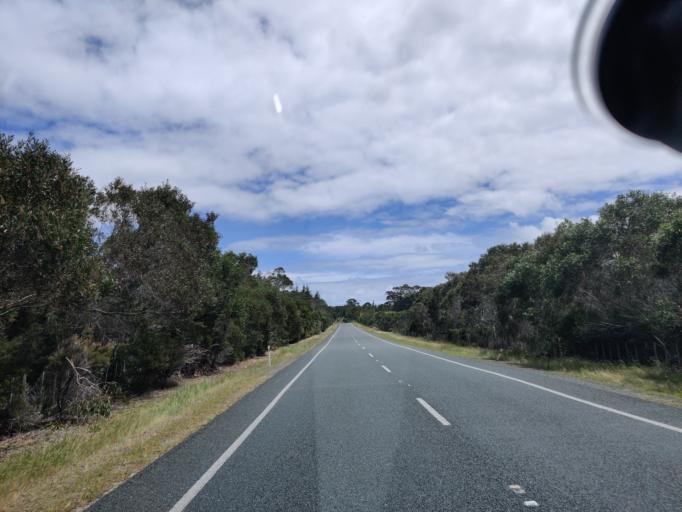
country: NZ
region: Northland
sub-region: Far North District
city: Kaitaia
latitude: -35.0182
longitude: 173.2146
